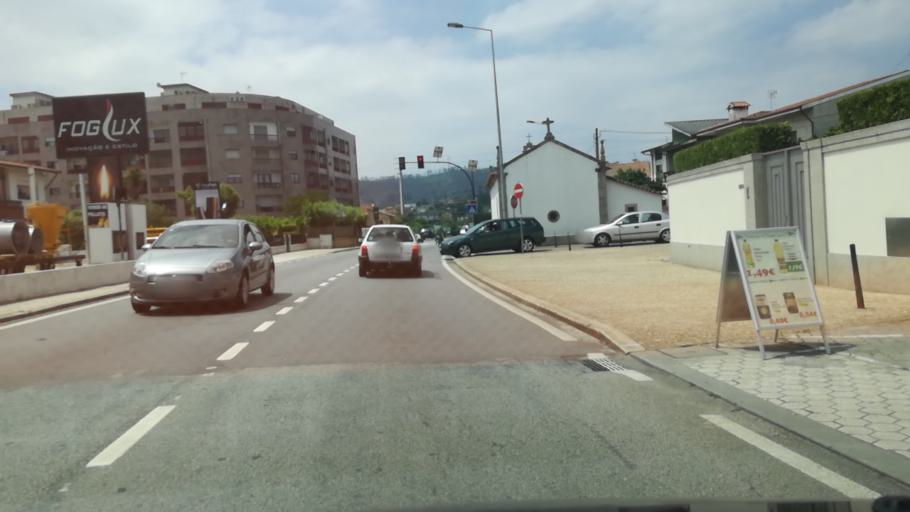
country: PT
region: Porto
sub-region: Trofa
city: Bougado
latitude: 41.3231
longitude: -8.5711
